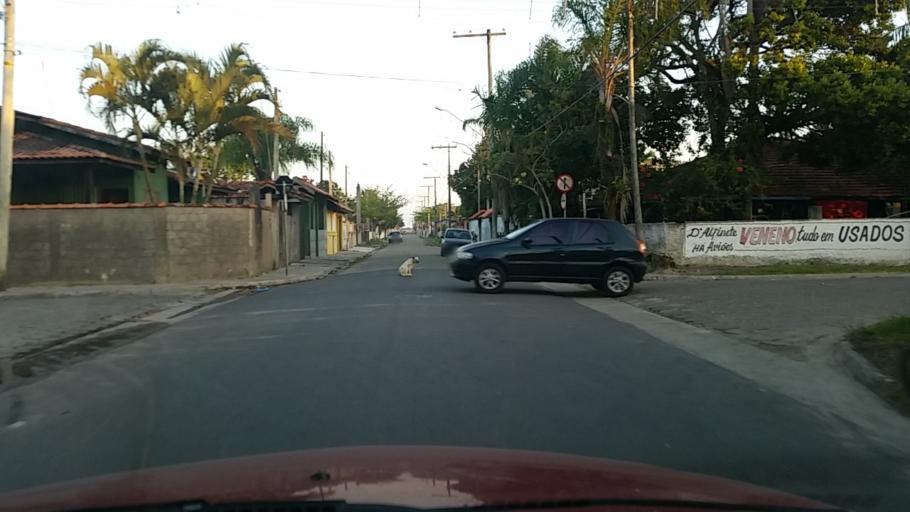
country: BR
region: Sao Paulo
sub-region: Iguape
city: Iguape
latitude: -24.7431
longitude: -47.5510
